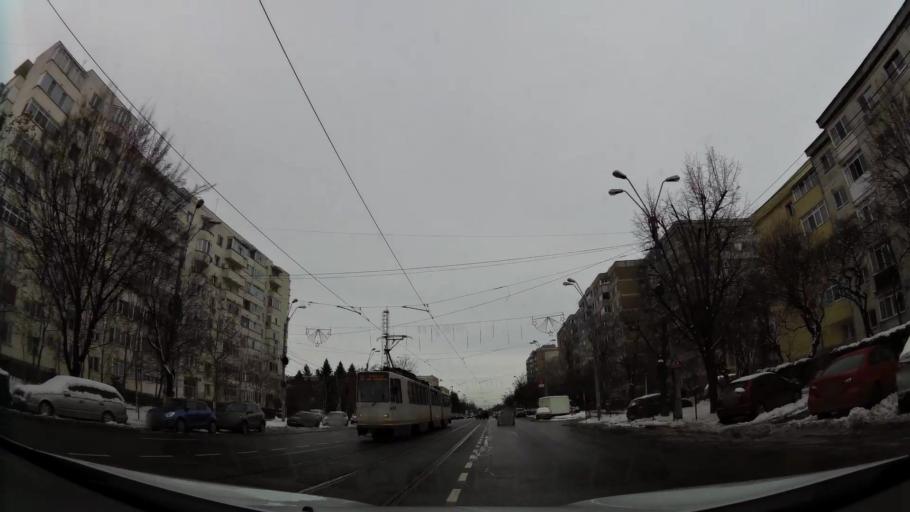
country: RO
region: Ilfov
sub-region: Comuna Popesti-Leordeni
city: Popesti-Leordeni
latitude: 44.3880
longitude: 26.1349
